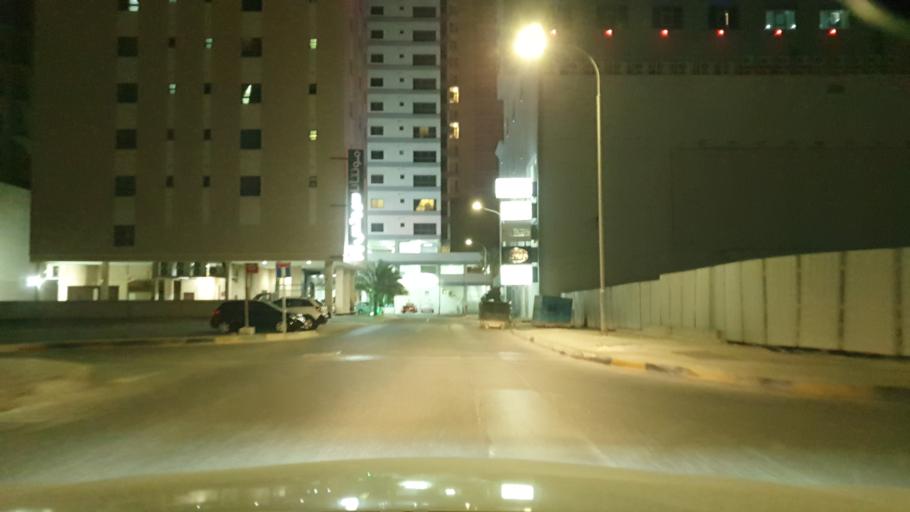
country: BH
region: Manama
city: Manama
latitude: 26.2189
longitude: 50.6059
